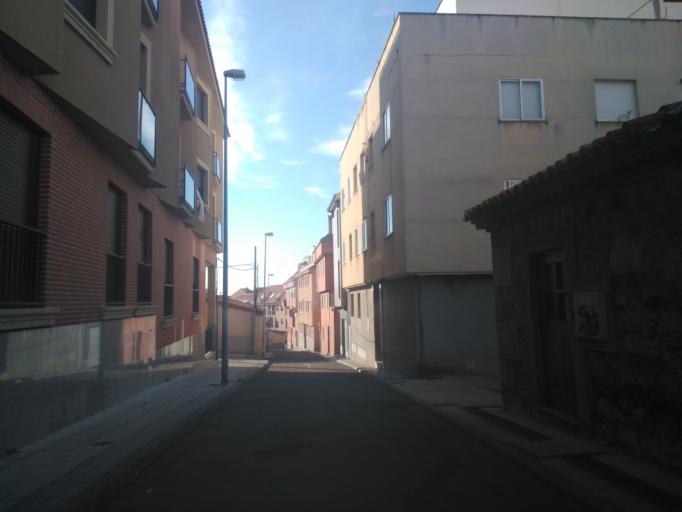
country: ES
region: Castille and Leon
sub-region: Provincia de Salamanca
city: Salamanca
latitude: 40.9780
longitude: -5.6754
